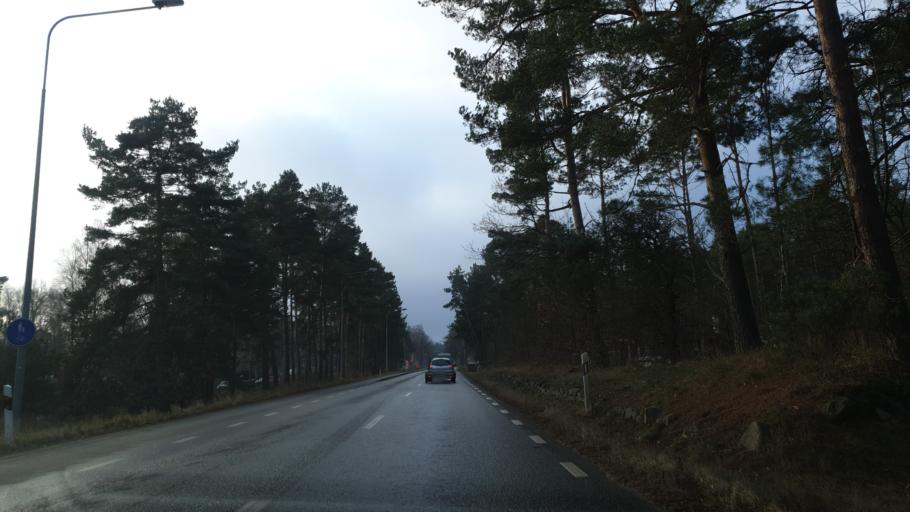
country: SE
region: Blekinge
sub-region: Karlshamns Kommun
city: Morrum
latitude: 56.1555
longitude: 14.6753
